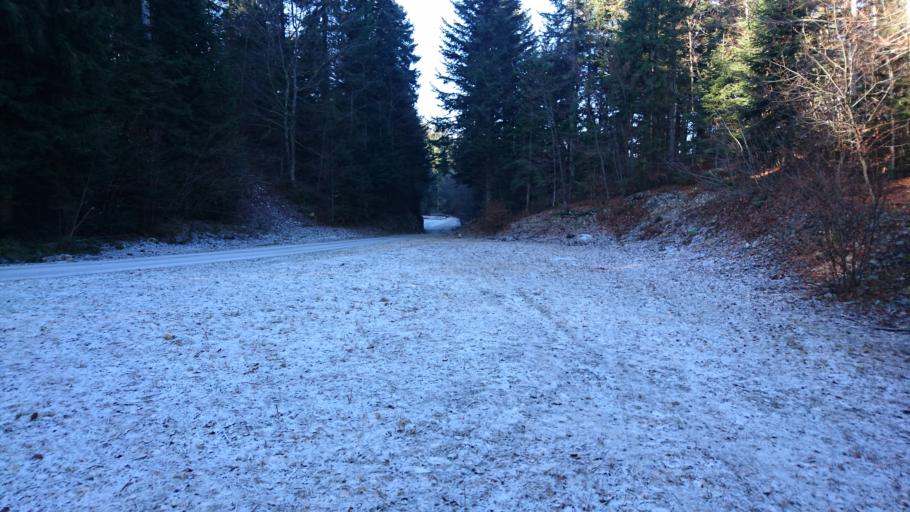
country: FR
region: Rhone-Alpes
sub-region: Departement de l'Ain
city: Oyonnax
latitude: 46.2200
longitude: 5.6881
